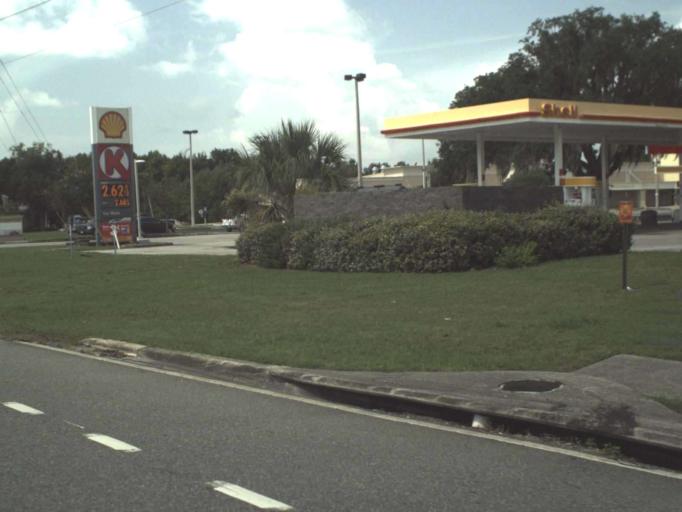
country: US
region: Florida
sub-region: Sumter County
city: Wildwood
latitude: 28.8469
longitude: -82.0455
